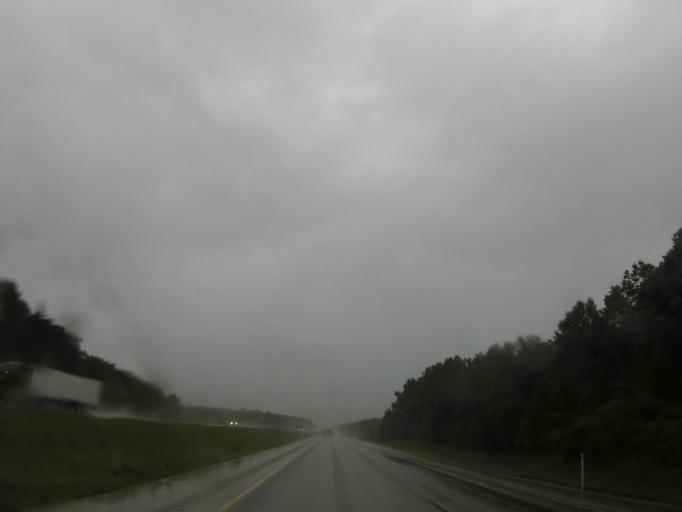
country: US
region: Illinois
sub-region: Johnson County
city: Goreville
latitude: 37.5175
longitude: -88.9114
